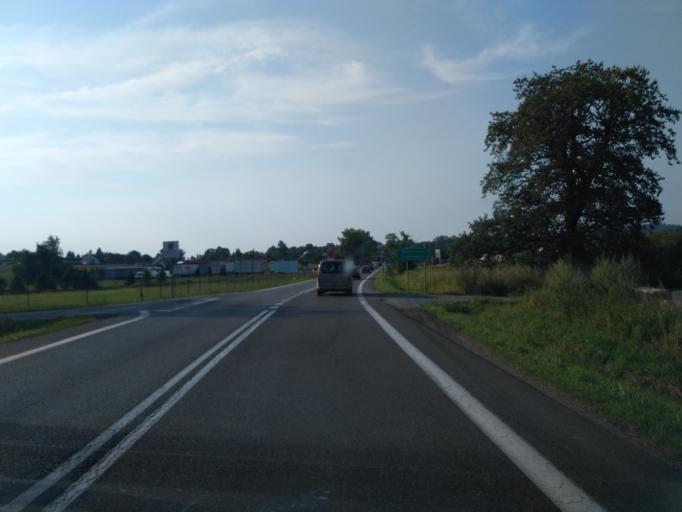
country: PL
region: Subcarpathian Voivodeship
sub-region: Powiat sanocki
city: Strachocina
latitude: 49.6112
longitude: 22.1180
